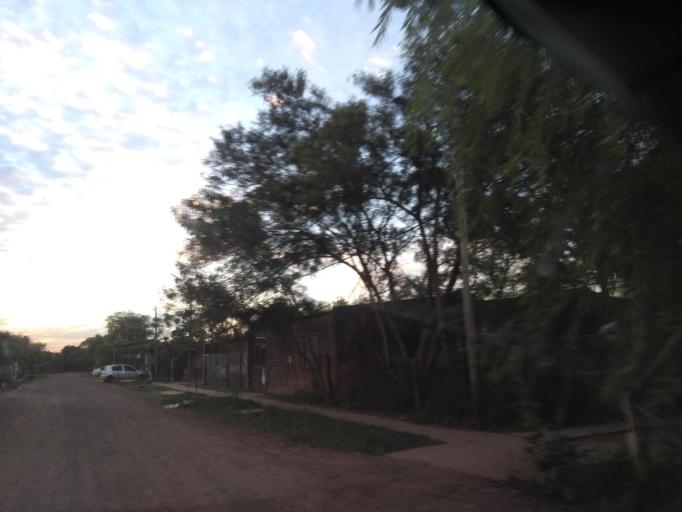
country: AR
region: Chaco
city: Fontana
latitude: -27.4113
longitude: -59.0510
